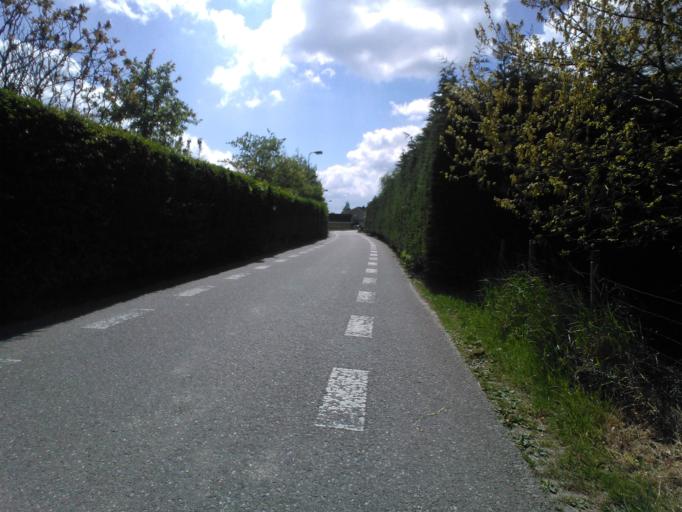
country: NL
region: South Holland
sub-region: Gemeente Hendrik-Ido-Ambacht
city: Hendrik-Ido-Ambacht
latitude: 51.8536
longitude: 4.6228
